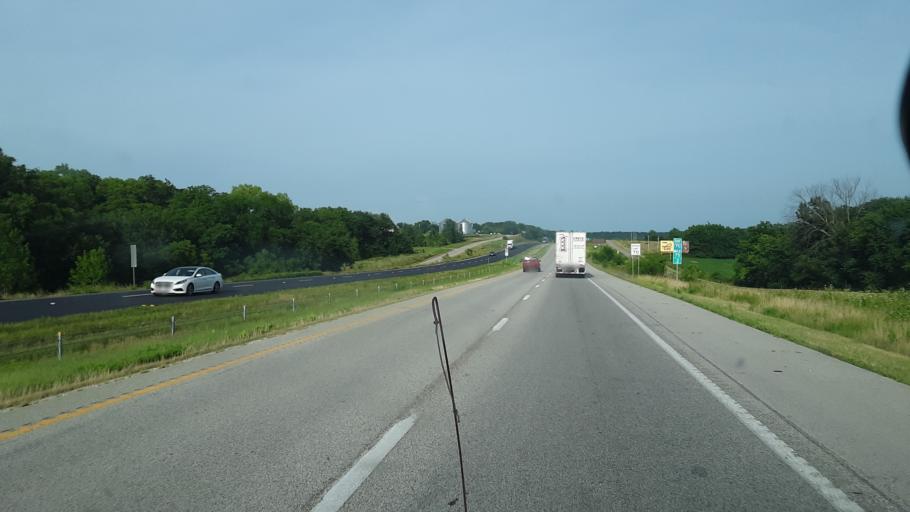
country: US
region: Missouri
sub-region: Saline County
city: Sweet Springs
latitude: 38.9705
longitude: -93.2626
